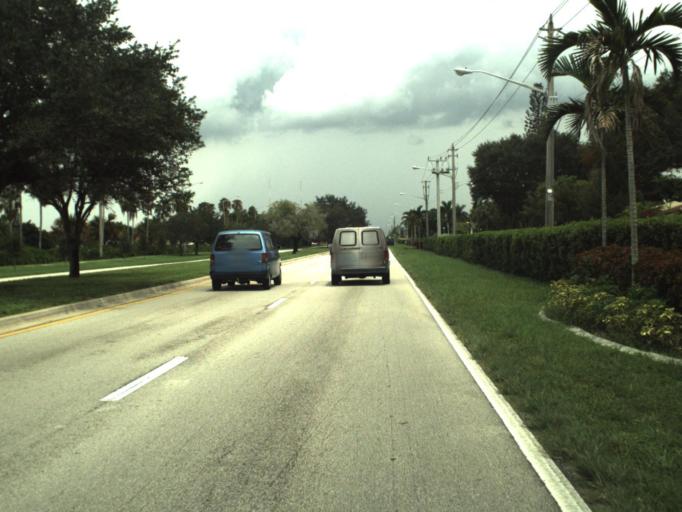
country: US
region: Florida
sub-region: Broward County
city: Cooper City
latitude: 26.0297
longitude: -80.2867
